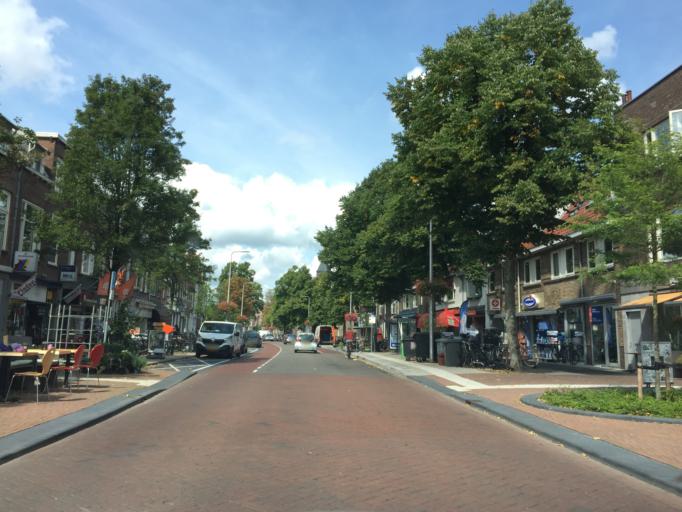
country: NL
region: Utrecht
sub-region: Gemeente Utrecht
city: Utrecht
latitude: 52.0828
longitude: 5.1403
